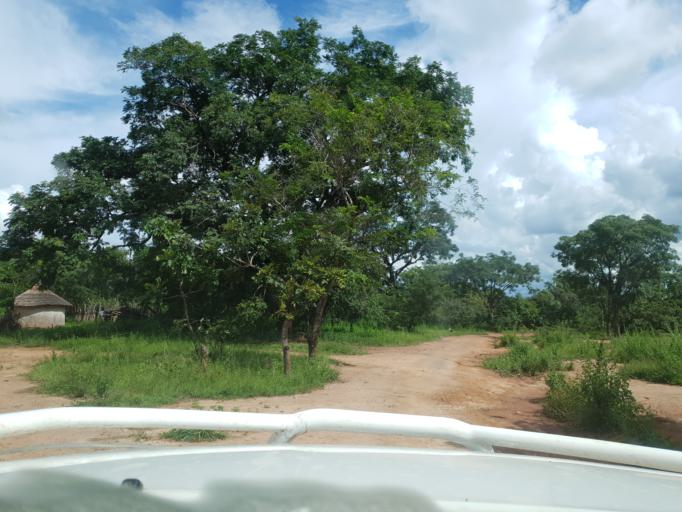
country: CI
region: Savanes
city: Tengrela
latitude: 10.4575
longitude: -6.7948
